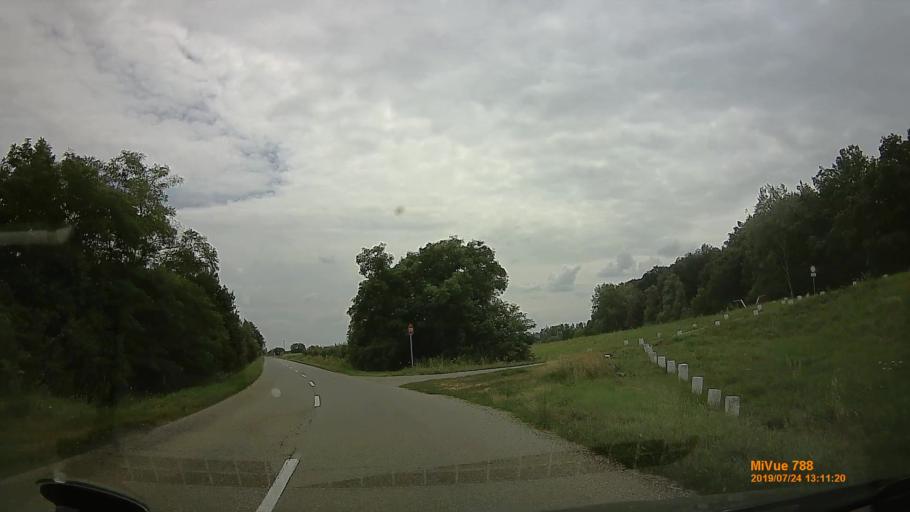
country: HU
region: Szabolcs-Szatmar-Bereg
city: Vasarosnameny
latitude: 48.1665
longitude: 22.3378
